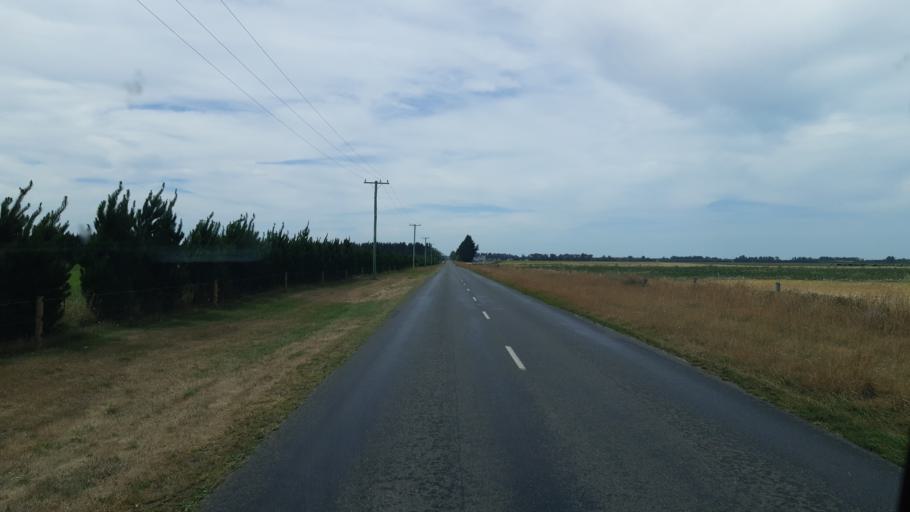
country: NZ
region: Canterbury
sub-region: Ashburton District
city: Tinwald
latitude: -43.9328
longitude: 171.6507
